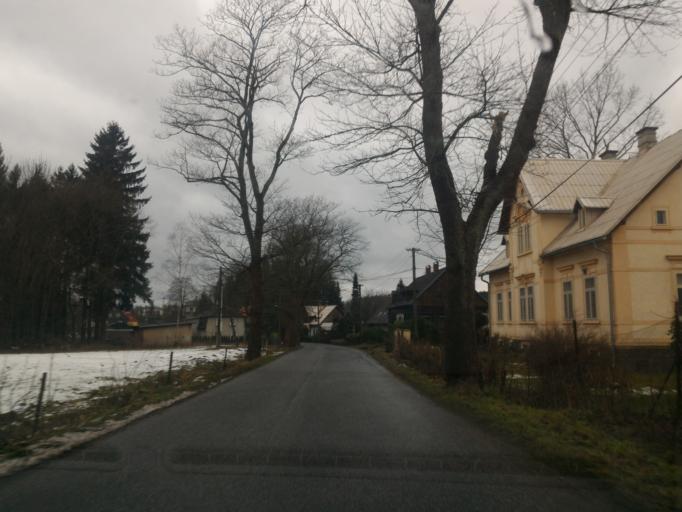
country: CZ
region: Ustecky
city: Stare Krecany
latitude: 50.9332
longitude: 14.4809
